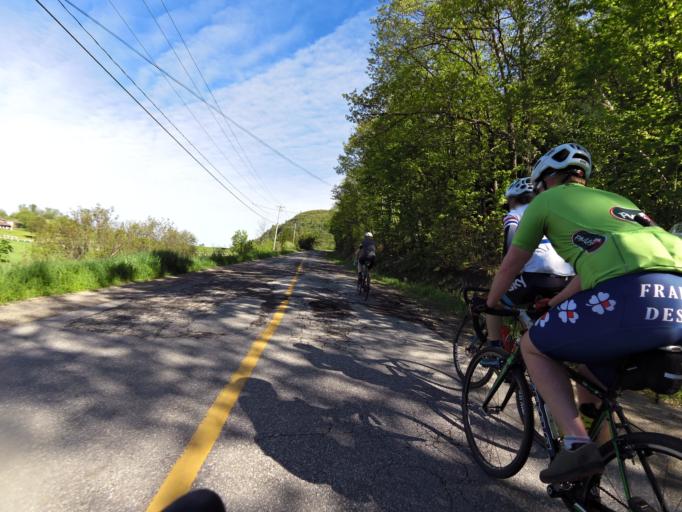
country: CA
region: Quebec
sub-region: Outaouais
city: Wakefield
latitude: 45.6711
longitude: -75.8746
